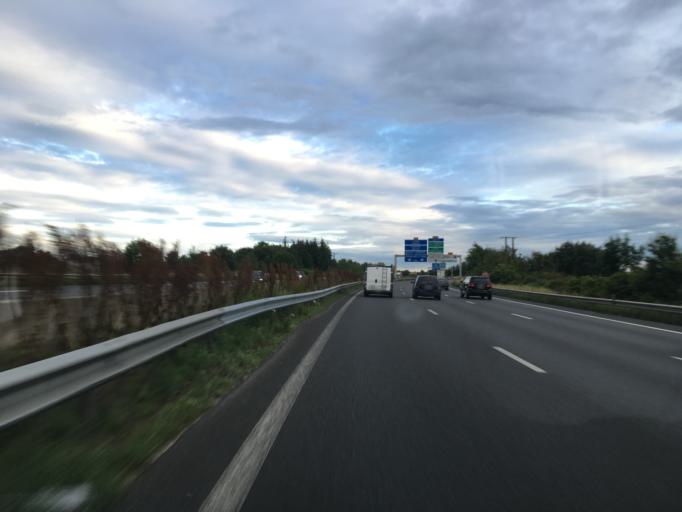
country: FR
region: Ile-de-France
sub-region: Departement de Seine-et-Marne
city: Brie-Comte-Robert
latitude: 48.6631
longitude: 2.6135
